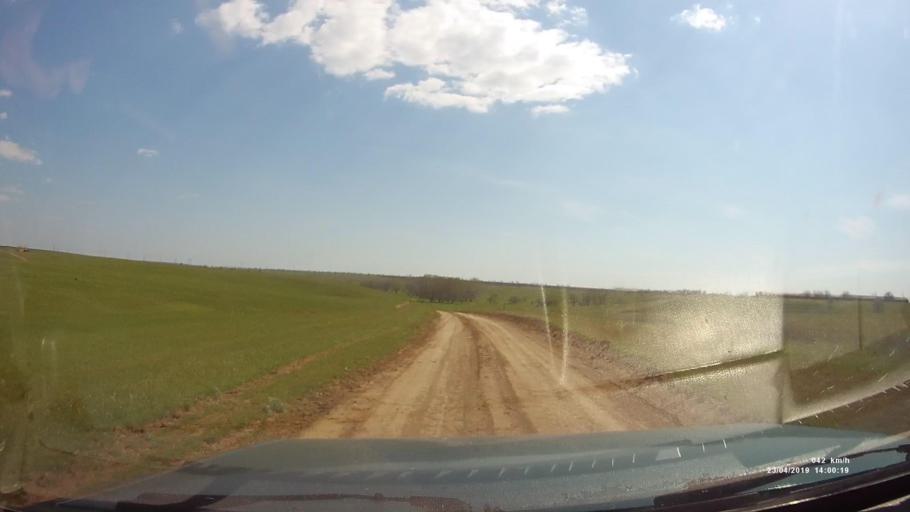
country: RU
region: Rostov
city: Remontnoye
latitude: 46.5603
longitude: 42.9468
